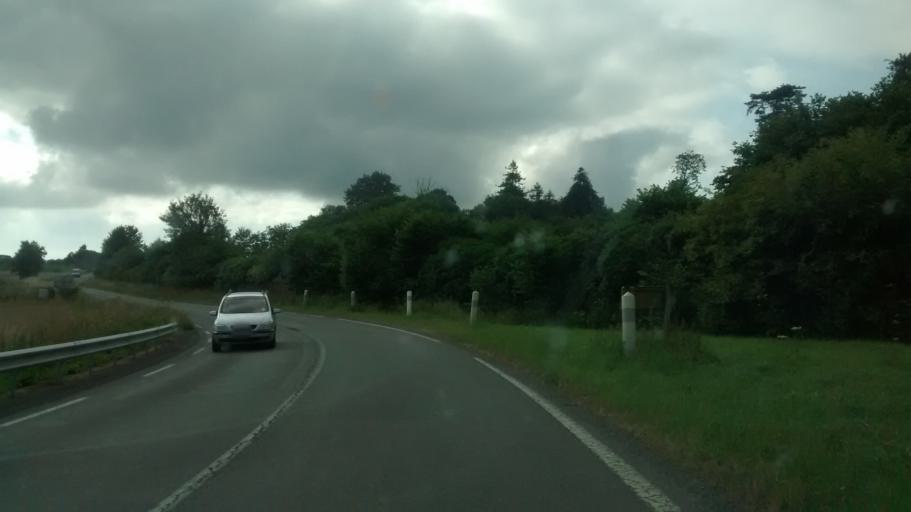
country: FR
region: Brittany
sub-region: Departement d'Ille-et-Vilaine
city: La Gouesniere
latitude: 48.5994
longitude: -1.8874
